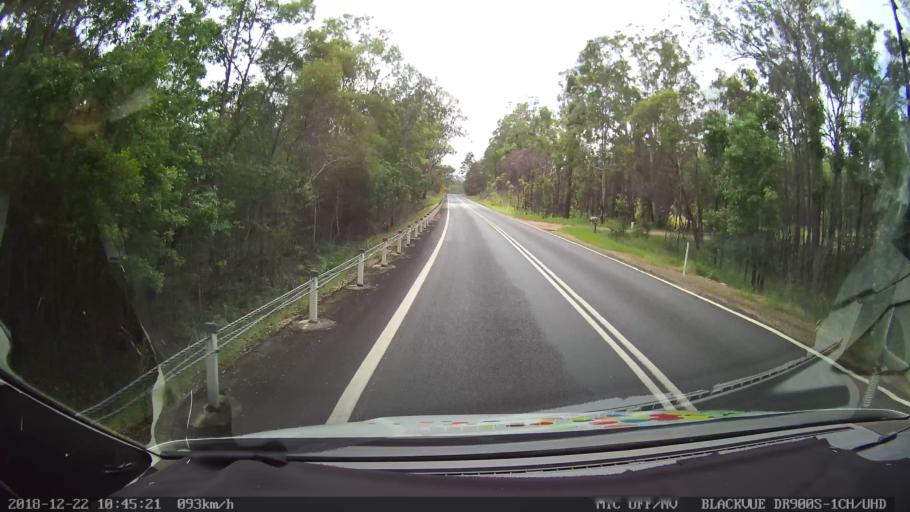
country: AU
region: New South Wales
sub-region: Clarence Valley
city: South Grafton
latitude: -29.6594
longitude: 152.8097
